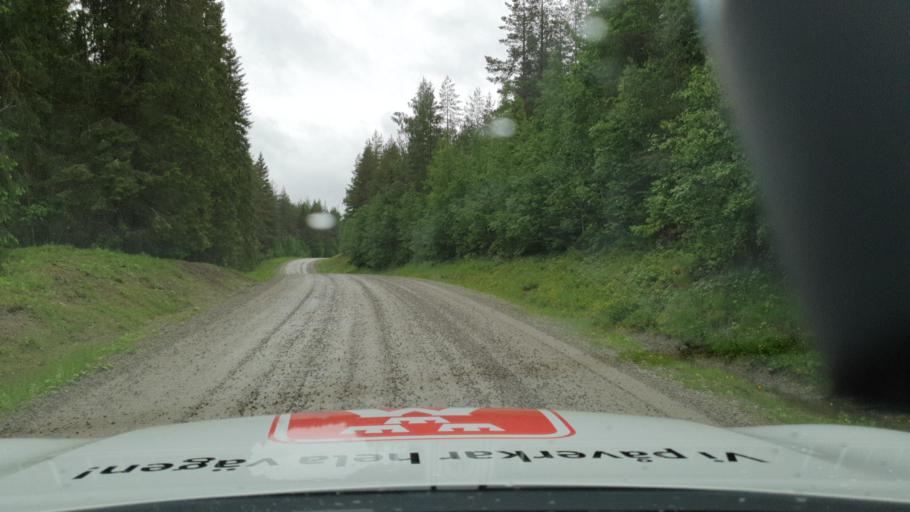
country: SE
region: Vaesterbotten
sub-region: Dorotea Kommun
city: Dorotea
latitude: 64.0449
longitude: 16.7414
